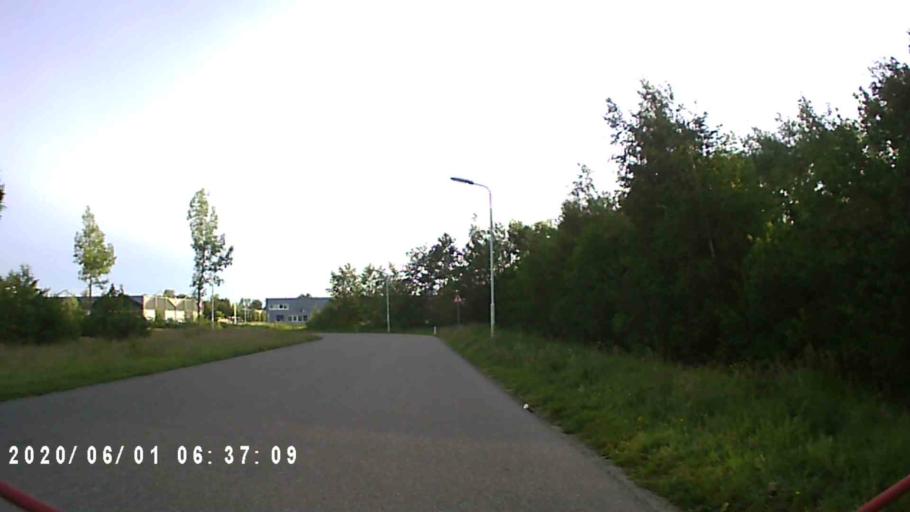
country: NL
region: Friesland
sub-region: Gemeente Kollumerland en Nieuwkruisland
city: Kollum
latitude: 53.2840
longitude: 6.1607
